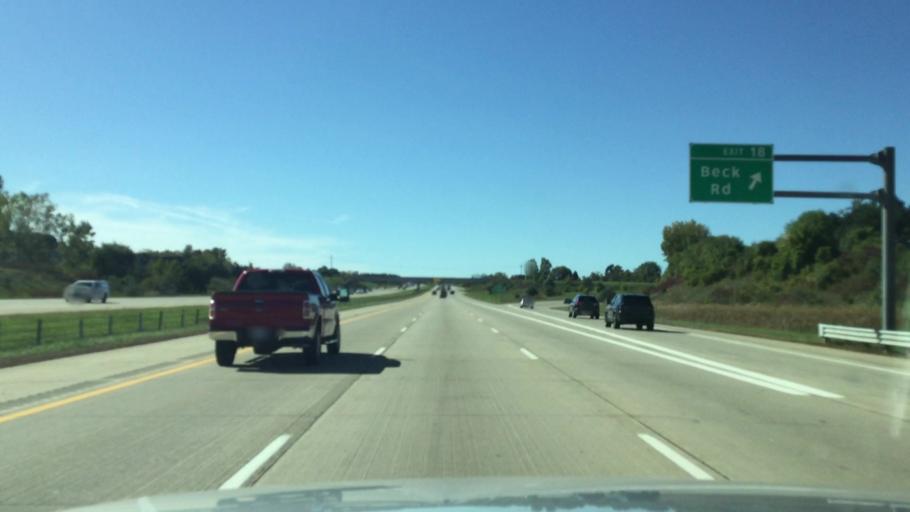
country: US
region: Michigan
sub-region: Wayne County
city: Plymouth
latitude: 42.3828
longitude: -83.5026
